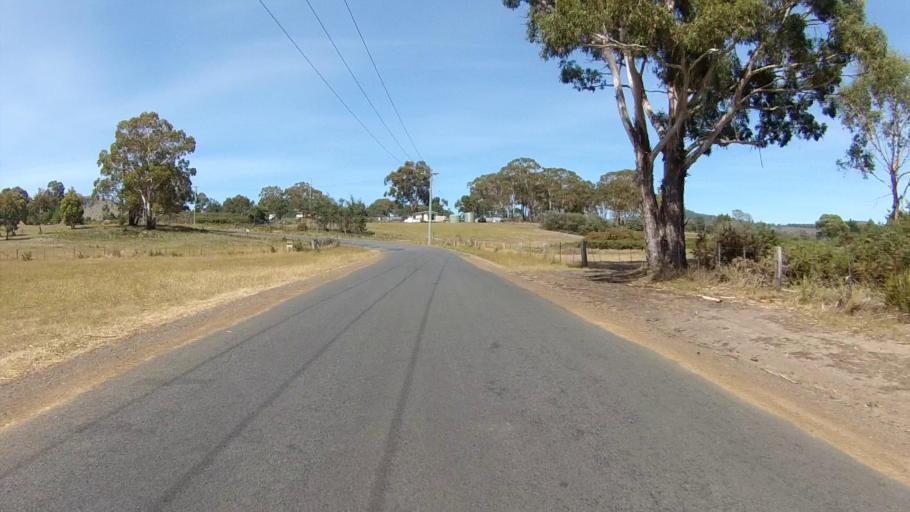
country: AU
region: Tasmania
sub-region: Sorell
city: Sorell
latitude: -42.6122
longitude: 147.7268
